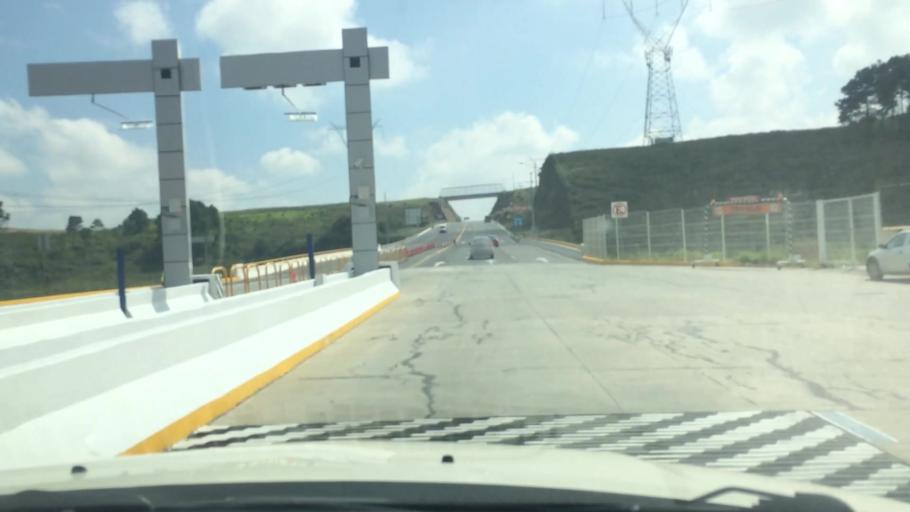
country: MX
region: Mexico
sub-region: Almoloya de Juarez
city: El Plan
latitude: 19.3814
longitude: -99.8045
